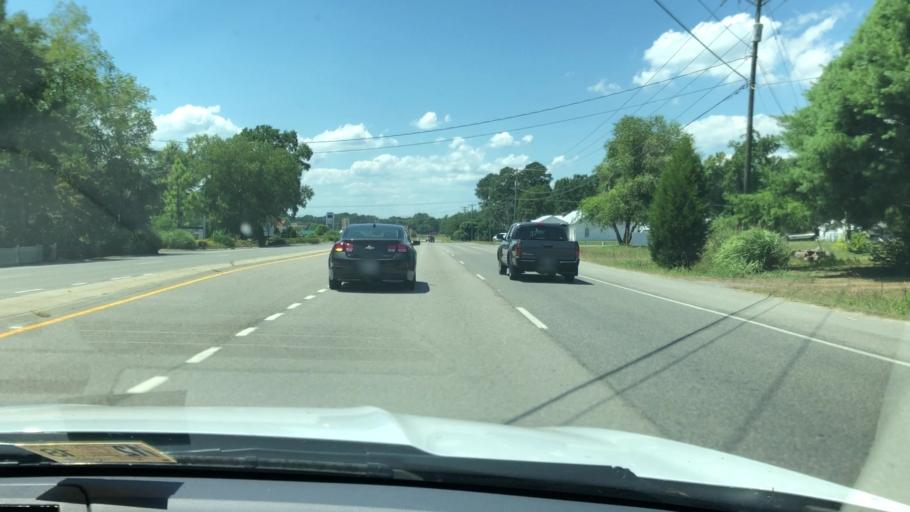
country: US
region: Virginia
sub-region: Middlesex County
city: Saluda
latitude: 37.5983
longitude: -76.5103
